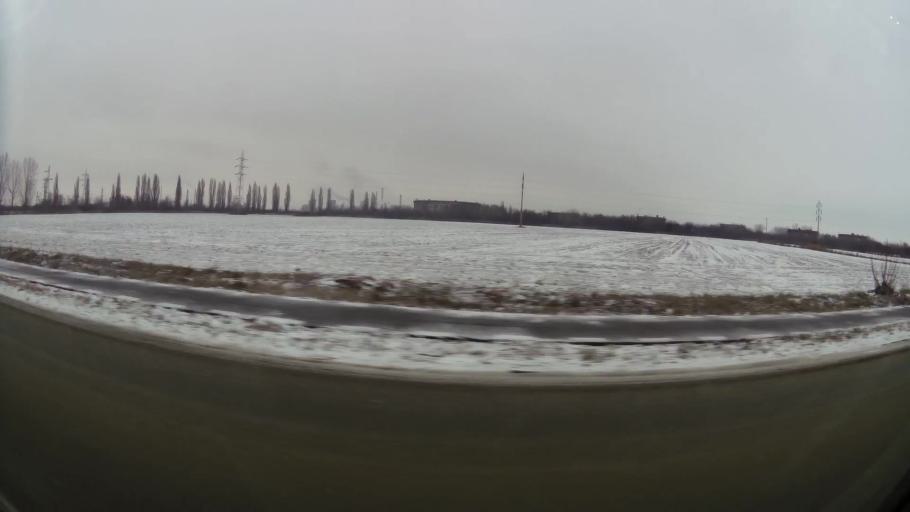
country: RO
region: Prahova
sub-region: Comuna Berceni
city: Corlatesti
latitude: 44.9294
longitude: 26.0656
